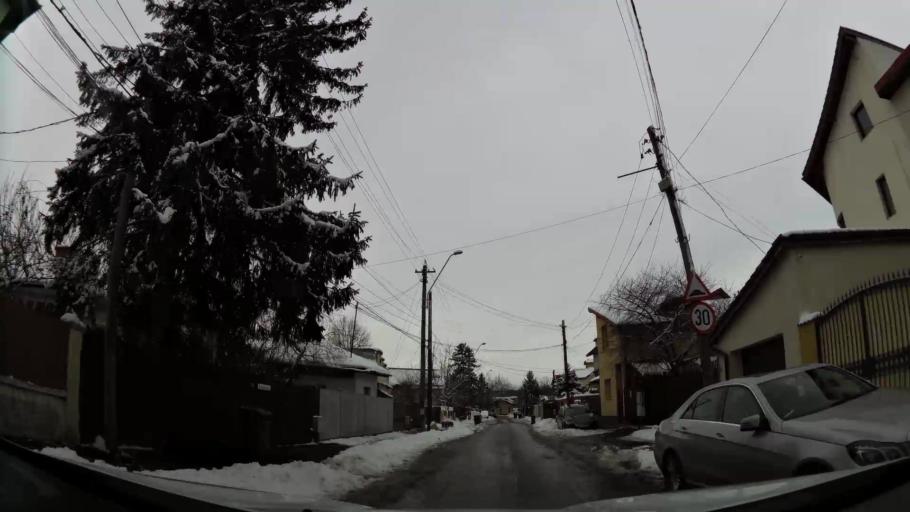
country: RO
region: Bucuresti
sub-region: Municipiul Bucuresti
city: Bucuresti
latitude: 44.3949
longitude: 26.1069
